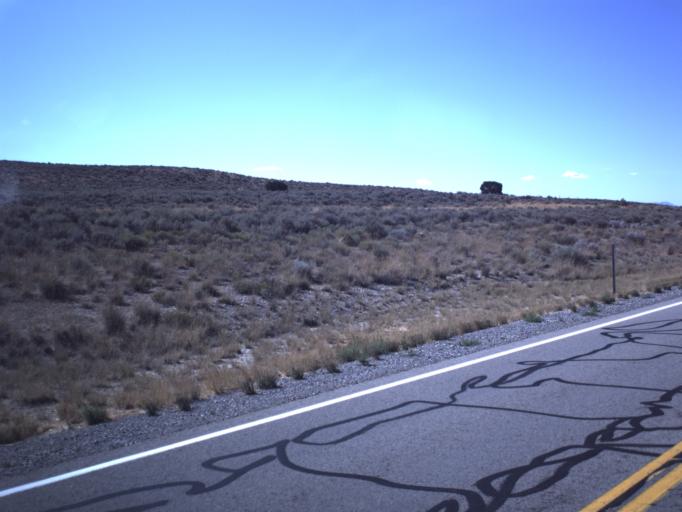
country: US
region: Utah
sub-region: Tooele County
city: Tooele
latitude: 40.4356
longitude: -112.3746
